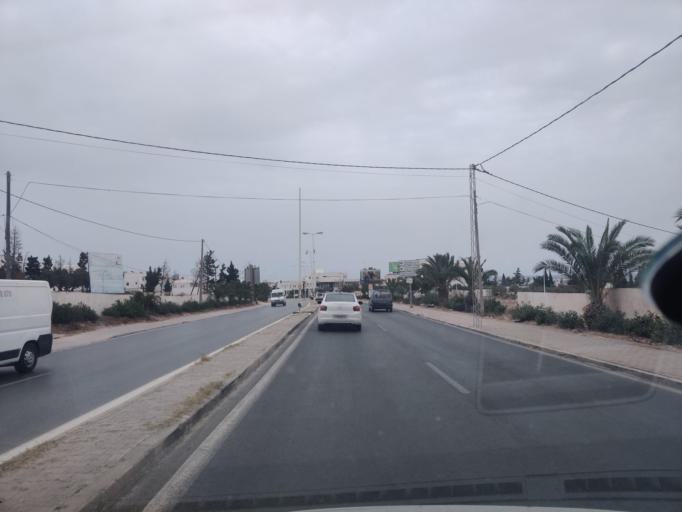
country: TN
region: Nabul
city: Al Hammamat
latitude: 36.4078
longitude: 10.6348
